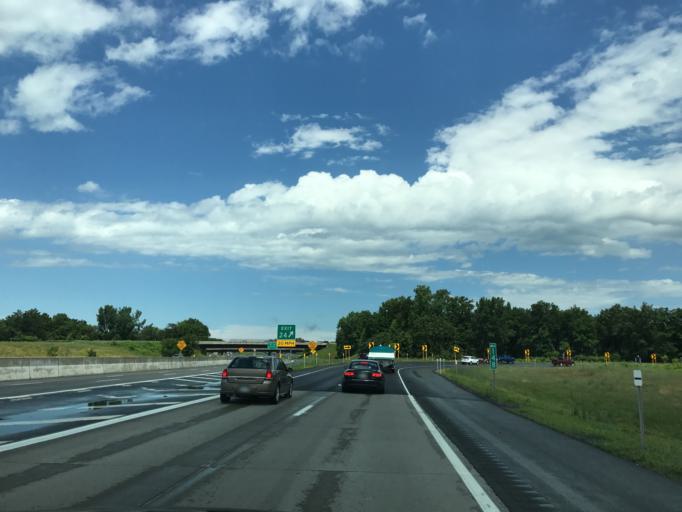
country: US
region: New York
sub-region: Albany County
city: McKownville
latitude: 42.6994
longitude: -73.8462
